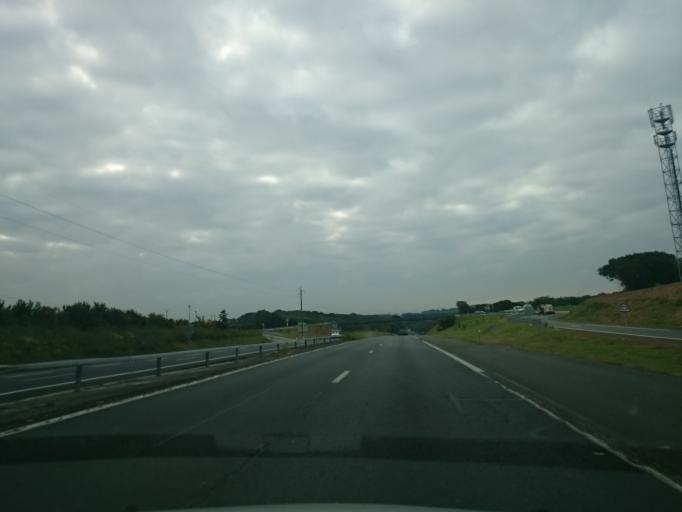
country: FR
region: Brittany
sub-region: Departement du Finistere
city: Loperhet
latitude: 48.3830
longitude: -4.3088
